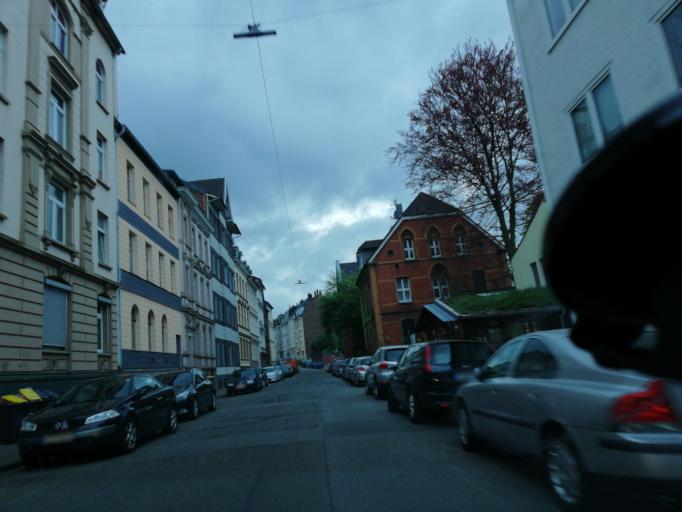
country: DE
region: North Rhine-Westphalia
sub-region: Regierungsbezirk Dusseldorf
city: Wuppertal
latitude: 51.2700
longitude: 7.2258
